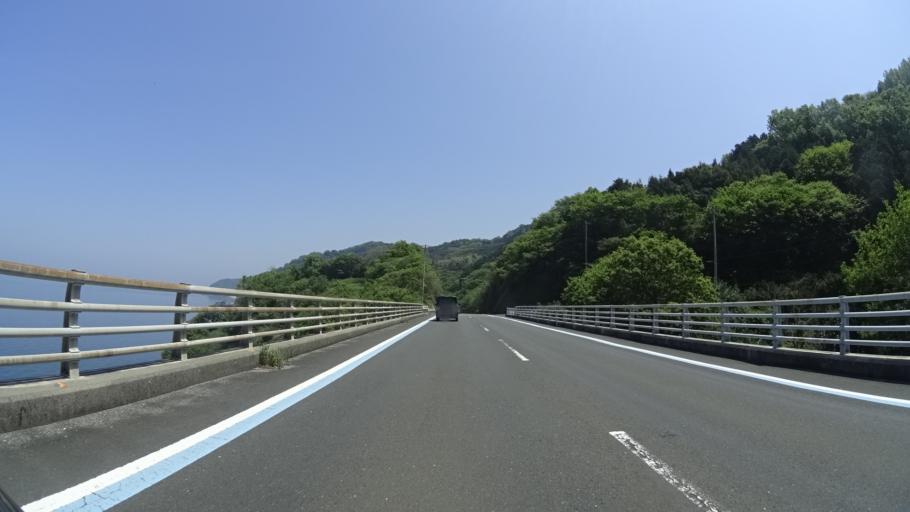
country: JP
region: Ehime
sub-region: Nishiuwa-gun
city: Ikata-cho
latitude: 33.5472
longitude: 132.4222
